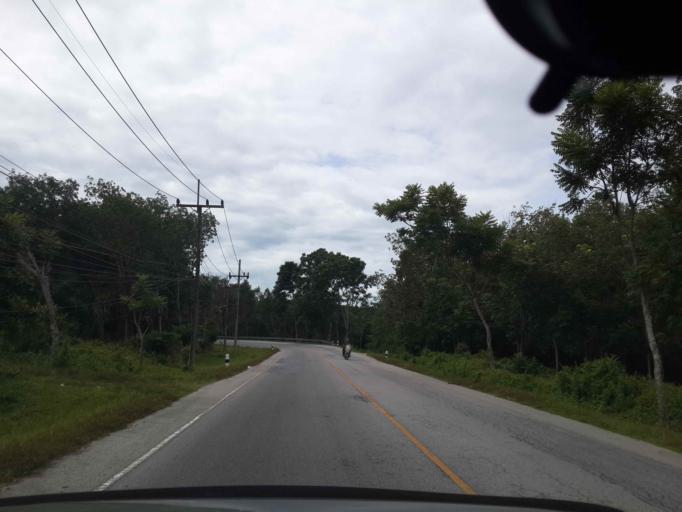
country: TH
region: Narathiwat
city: Rueso
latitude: 6.3816
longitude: 101.5185
